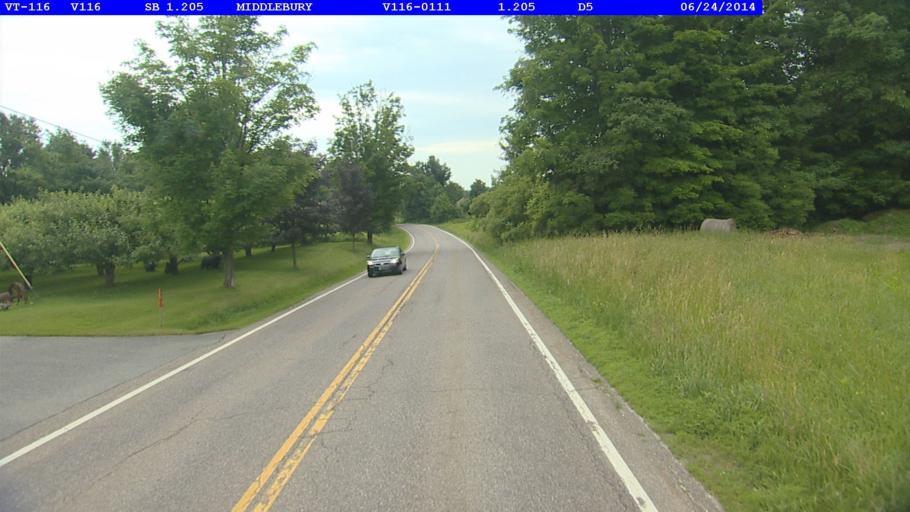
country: US
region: Vermont
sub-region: Addison County
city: Middlebury (village)
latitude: 43.9821
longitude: -73.1048
